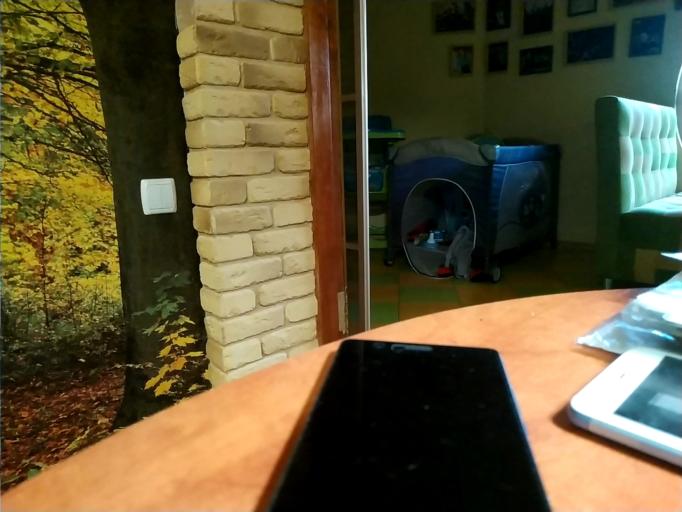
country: RU
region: Orjol
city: Znamenskoye
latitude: 53.5531
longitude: 35.4872
